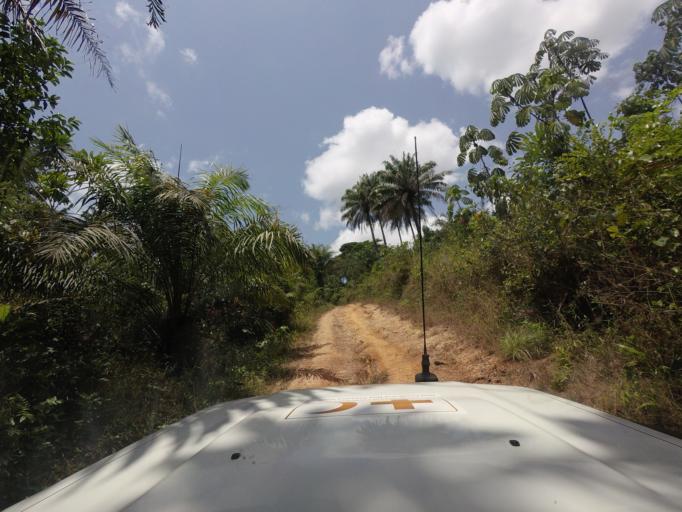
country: GN
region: Nzerekore
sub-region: Yomou
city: Yomou
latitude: 7.3757
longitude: -9.3202
